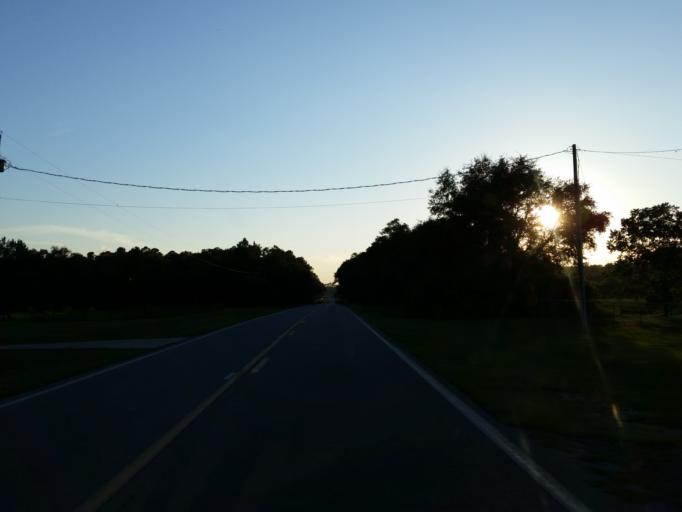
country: US
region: Georgia
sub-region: Berrien County
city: Nashville
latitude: 31.1862
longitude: -83.1723
